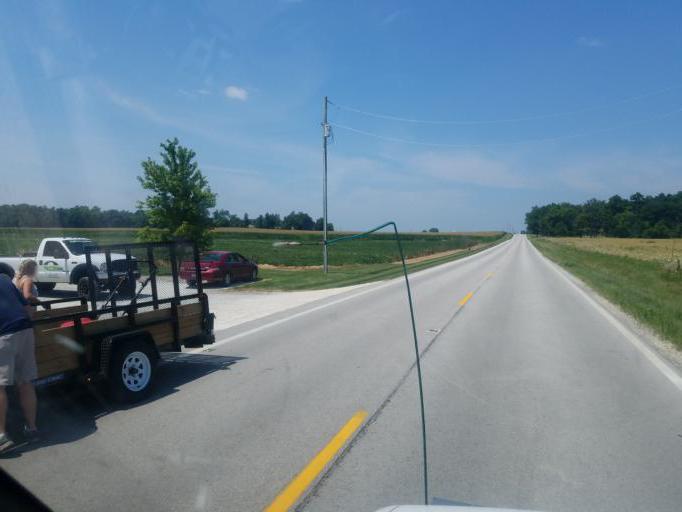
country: US
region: Ohio
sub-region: Auglaize County
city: Minster
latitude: 40.4099
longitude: -84.4338
